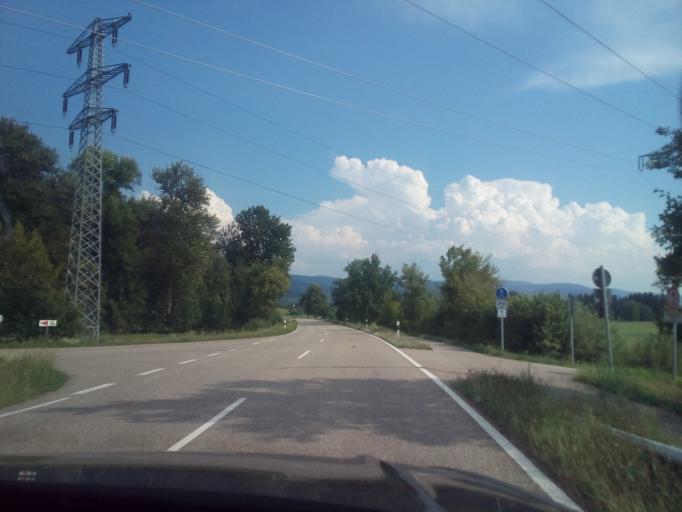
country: DE
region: Baden-Wuerttemberg
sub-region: Karlsruhe Region
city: Sinzheim
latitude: 48.7779
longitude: 8.1529
